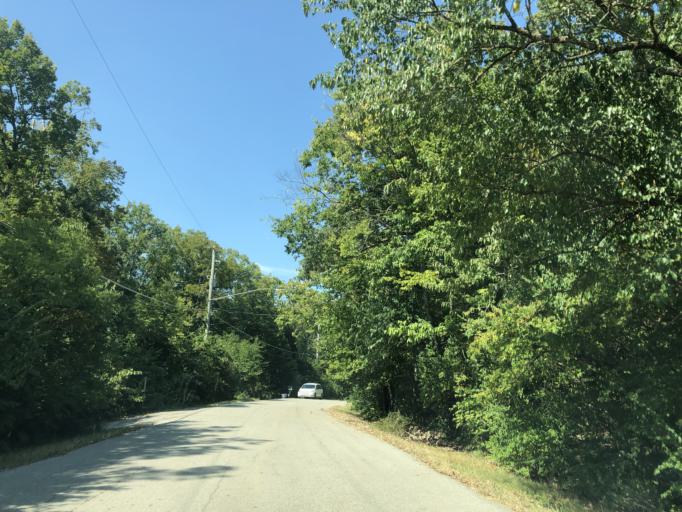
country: US
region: Tennessee
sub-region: Davidson County
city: Oak Hill
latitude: 36.0876
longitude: -86.8112
